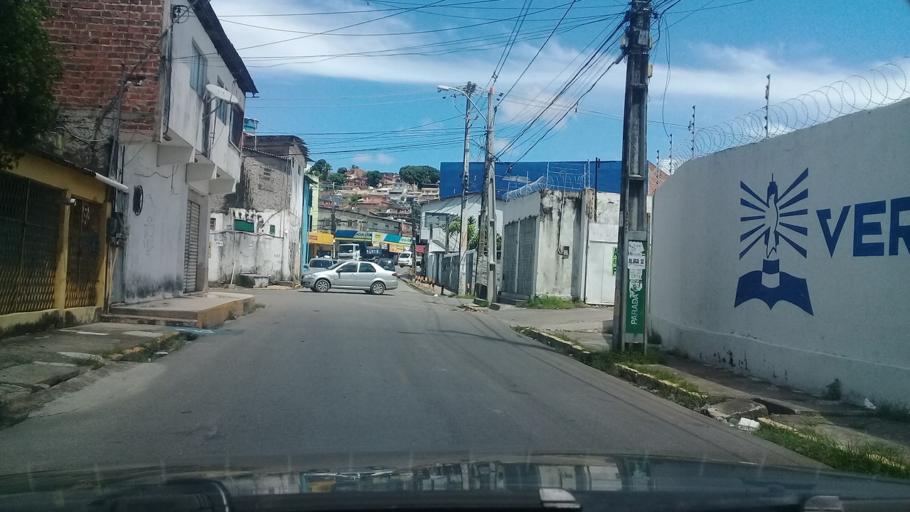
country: BR
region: Pernambuco
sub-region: Jaboatao Dos Guararapes
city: Jaboatao dos Guararapes
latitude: -8.1153
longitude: -34.9408
